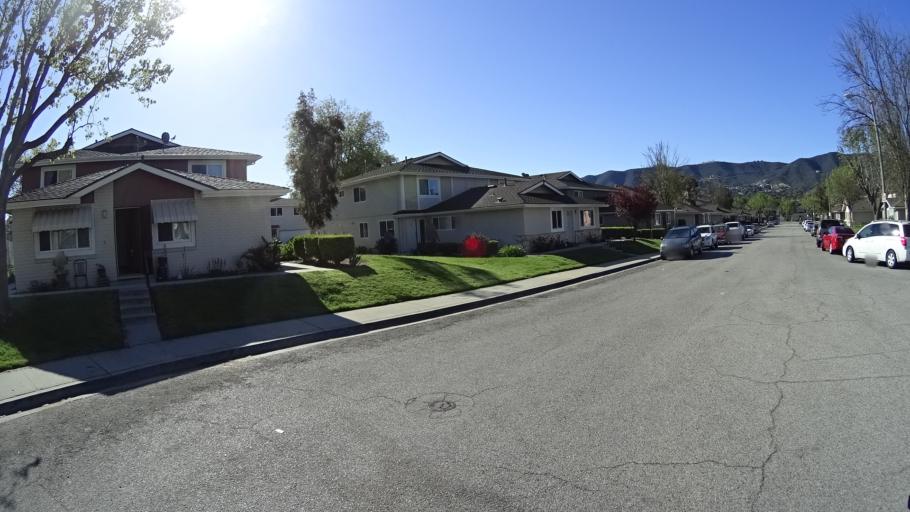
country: US
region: California
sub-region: Ventura County
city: Casa Conejo
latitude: 34.1882
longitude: -118.9143
